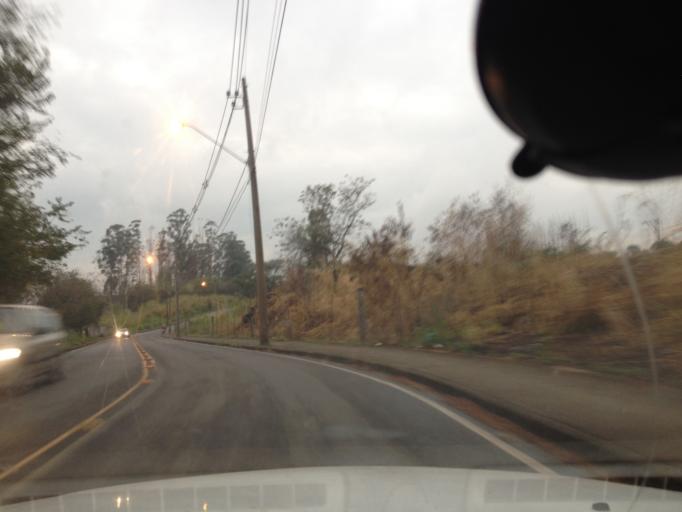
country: BR
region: Sao Paulo
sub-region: Salto
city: Salto
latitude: -23.2058
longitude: -47.2738
